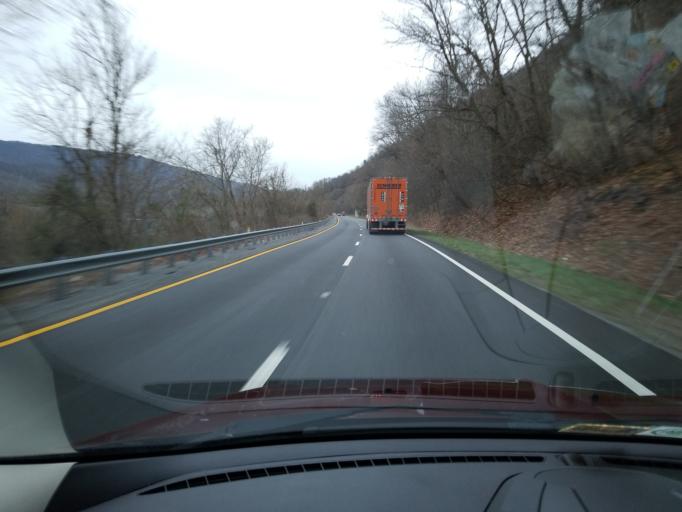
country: US
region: Virginia
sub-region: Giles County
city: Narrows
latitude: 37.3871
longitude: -80.8401
